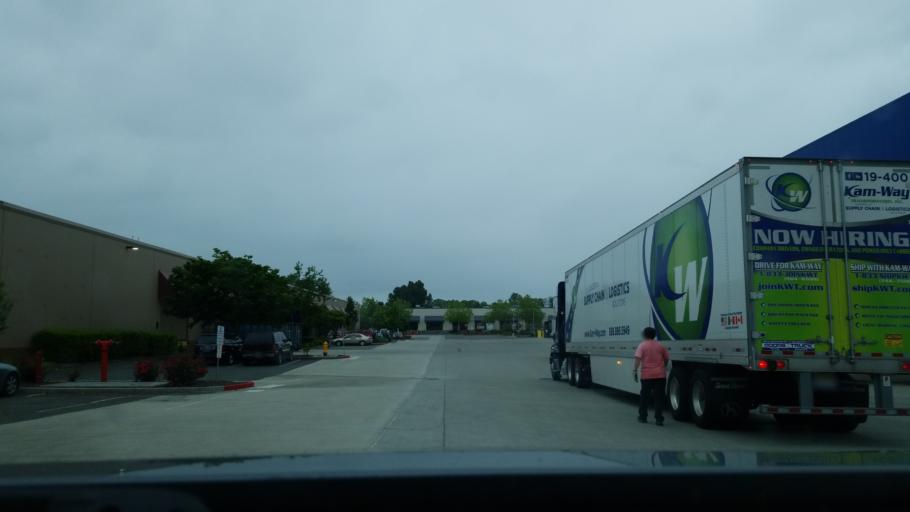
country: US
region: Washington
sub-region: King County
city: Renton
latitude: 47.4419
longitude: -122.2297
